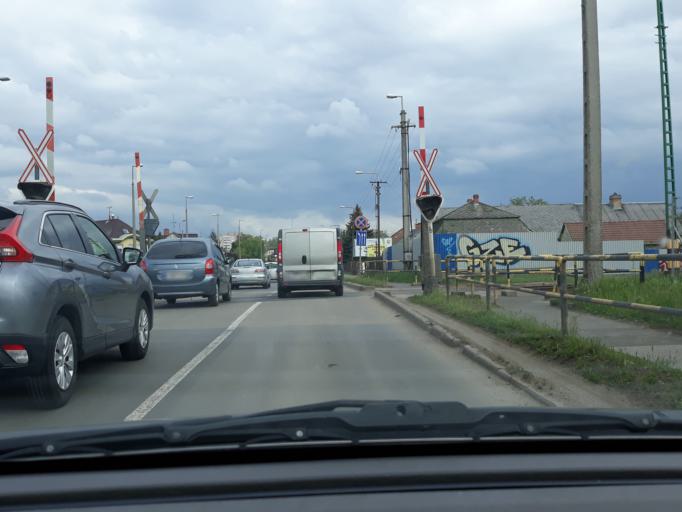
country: HU
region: Hajdu-Bihar
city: Debrecen
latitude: 47.5272
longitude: 21.5885
